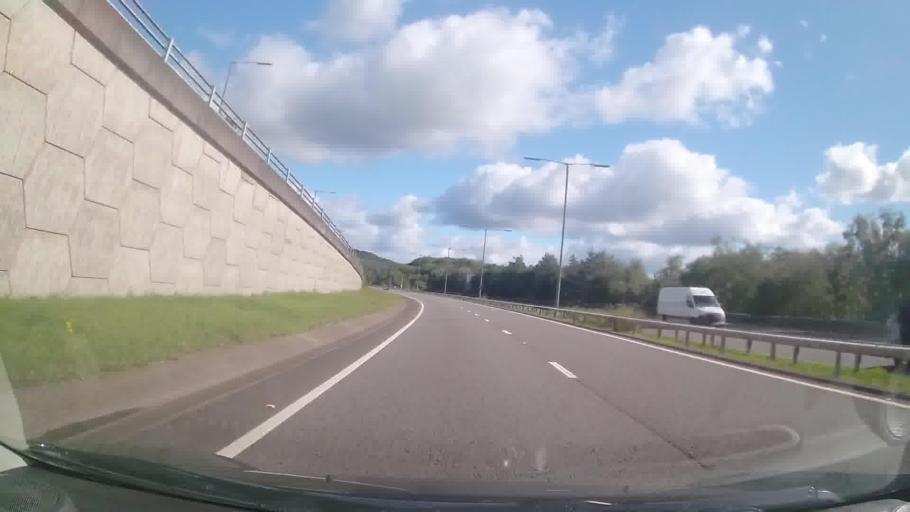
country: GB
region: Wales
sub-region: Neath Port Talbot
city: Neath
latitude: 51.6782
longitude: -3.7799
